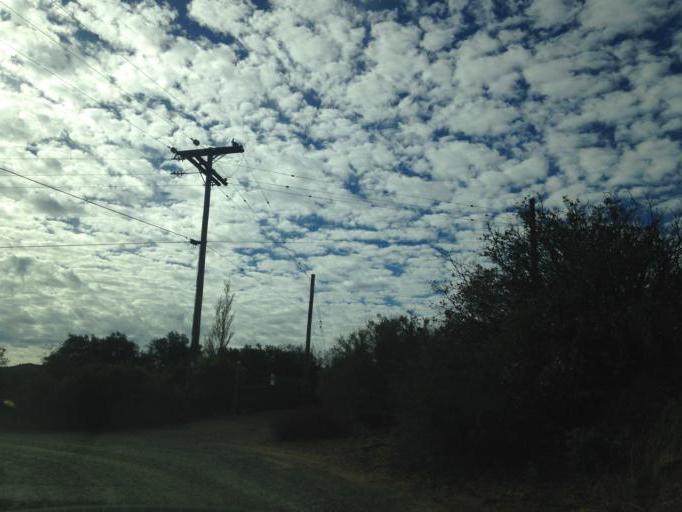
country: US
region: California
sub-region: San Diego County
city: Julian
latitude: 33.0319
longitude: -116.5572
